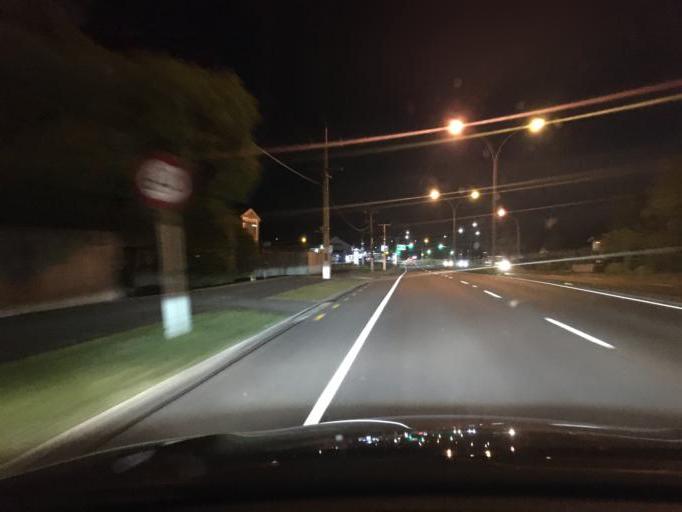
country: NZ
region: Waikato
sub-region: Hamilton City
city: Hamilton
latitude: -37.8156
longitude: 175.2828
